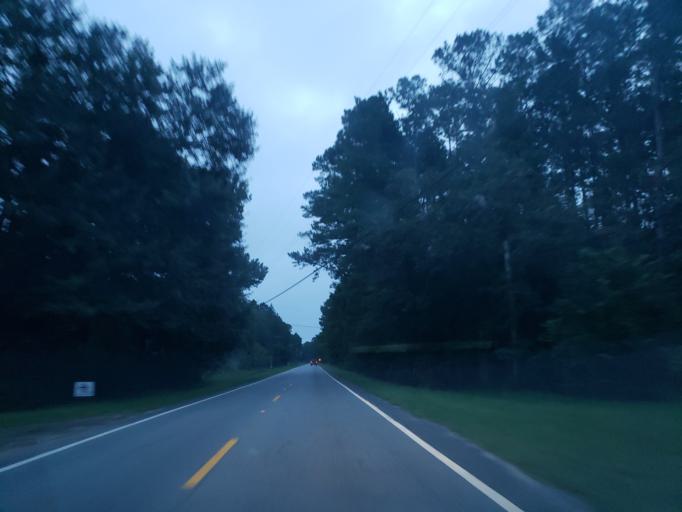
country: US
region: Georgia
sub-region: Chatham County
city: Bloomingdale
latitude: 32.0829
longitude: -81.3696
